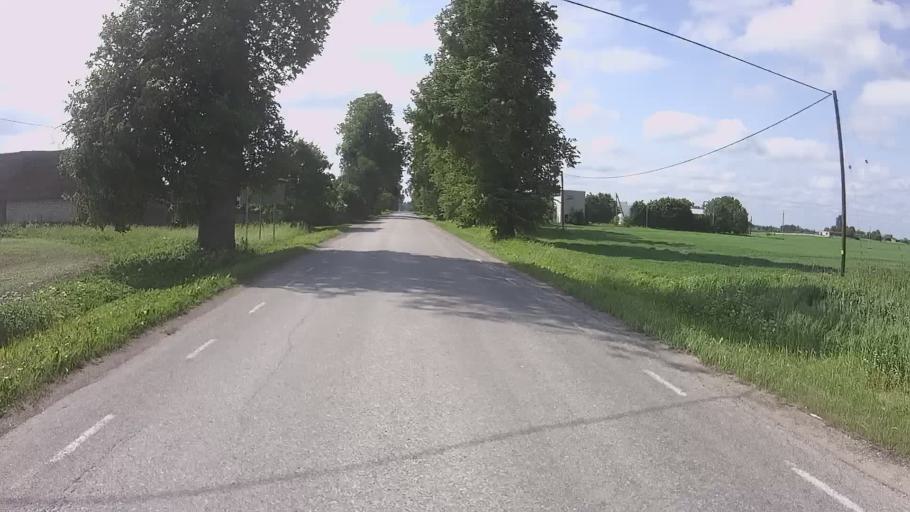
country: EE
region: Vorumaa
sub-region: Antsla vald
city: Vana-Antsla
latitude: 57.8672
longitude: 26.6086
